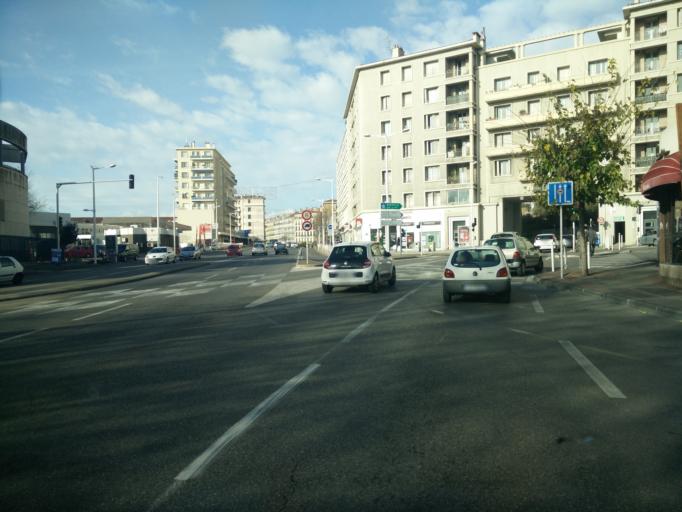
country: FR
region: Provence-Alpes-Cote d'Azur
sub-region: Departement du Var
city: Toulon
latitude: 43.1226
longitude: 5.9393
